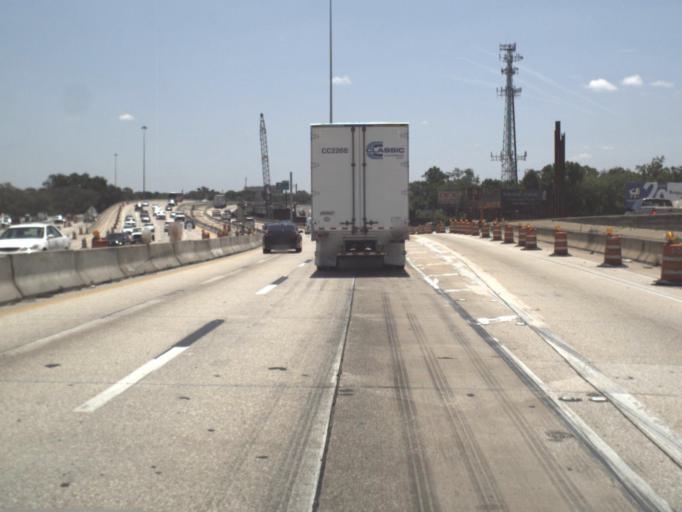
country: US
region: Florida
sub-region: Duval County
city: Jacksonville
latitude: 30.3120
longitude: -81.6504
